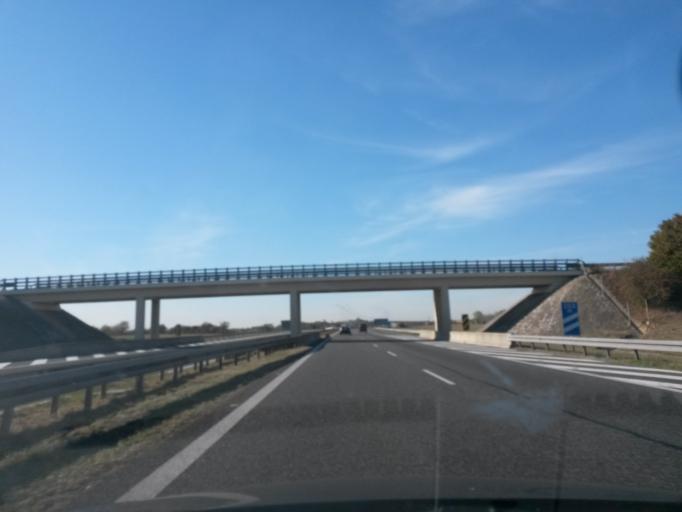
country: PL
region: Opole Voivodeship
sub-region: Powiat brzeski
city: Grodkow
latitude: 50.7770
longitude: 17.3586
